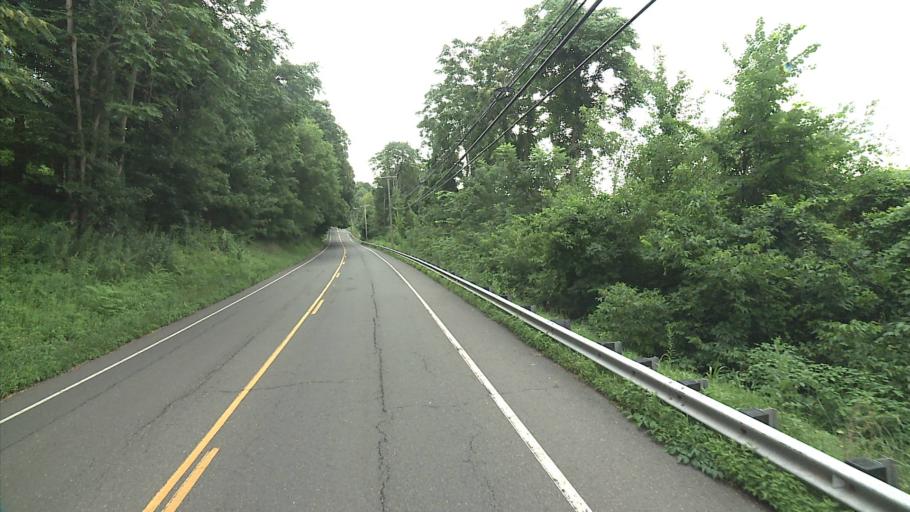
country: US
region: Connecticut
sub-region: Litchfield County
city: New Milford
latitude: 41.5601
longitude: -73.3907
